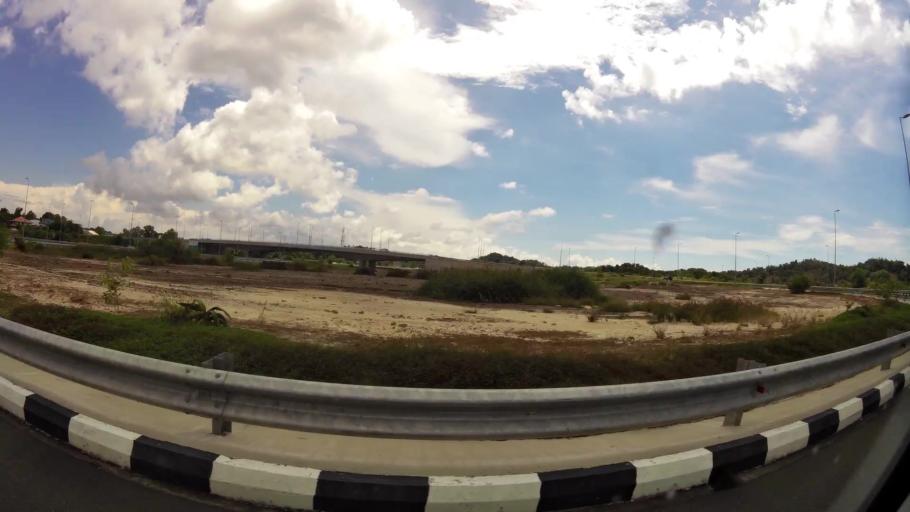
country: BN
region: Brunei and Muara
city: Bandar Seri Begawan
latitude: 4.9875
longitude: 114.9621
